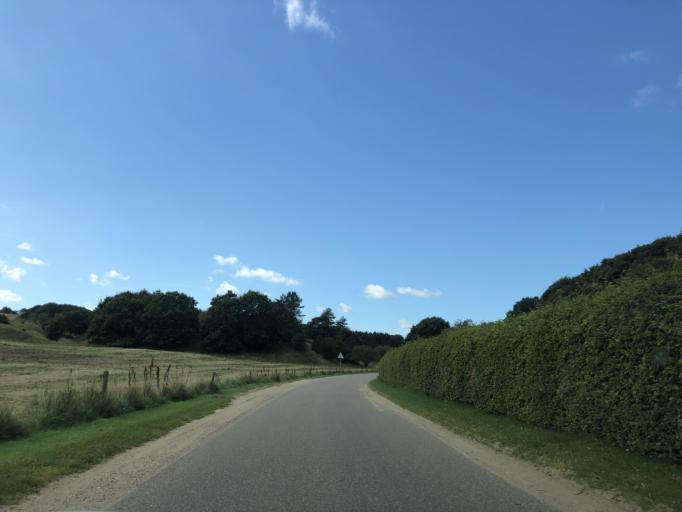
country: DK
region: Central Jutland
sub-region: Viborg Kommune
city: Viborg
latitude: 56.5657
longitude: 9.3214
